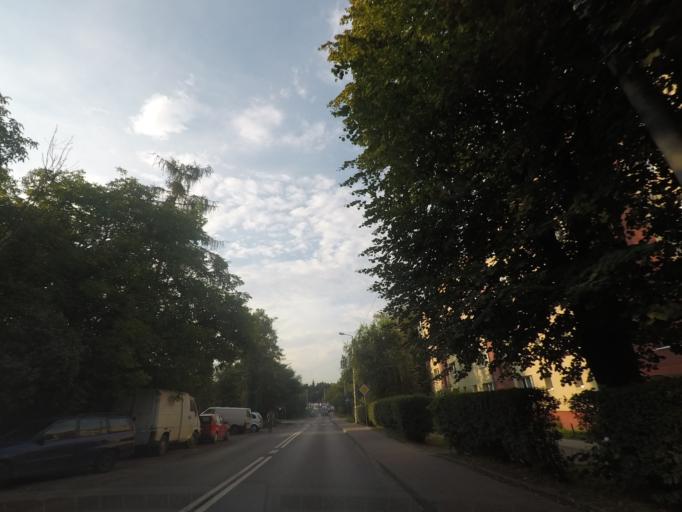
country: PL
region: Lesser Poland Voivodeship
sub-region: Powiat wielicki
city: Wieliczka
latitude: 49.9919
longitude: 20.0418
